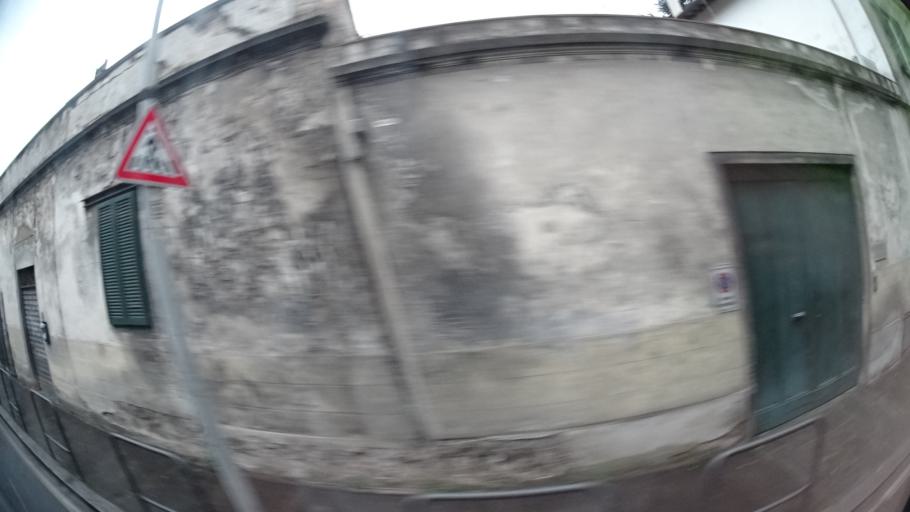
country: IT
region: Tuscany
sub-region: Province of Florence
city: Florence
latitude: 43.7524
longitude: 11.2386
